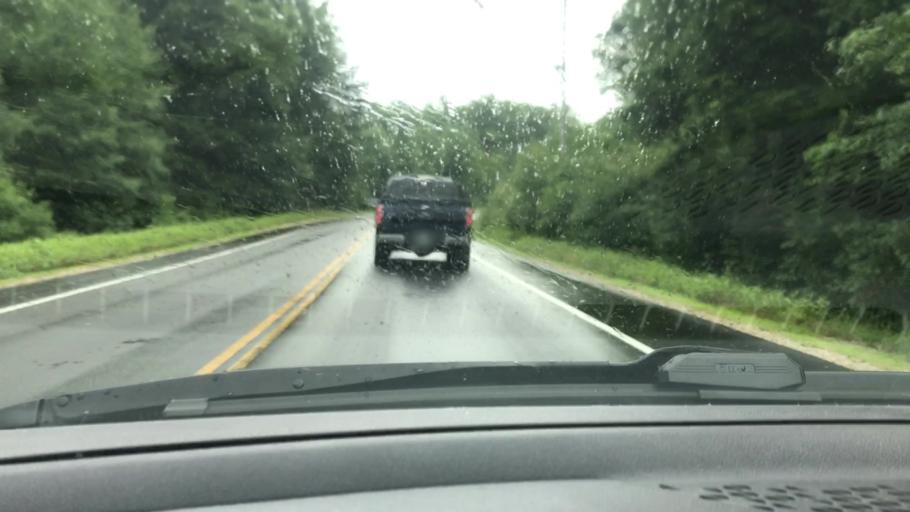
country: US
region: New Hampshire
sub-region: Rockingham County
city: Candia
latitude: 43.1394
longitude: -71.2355
